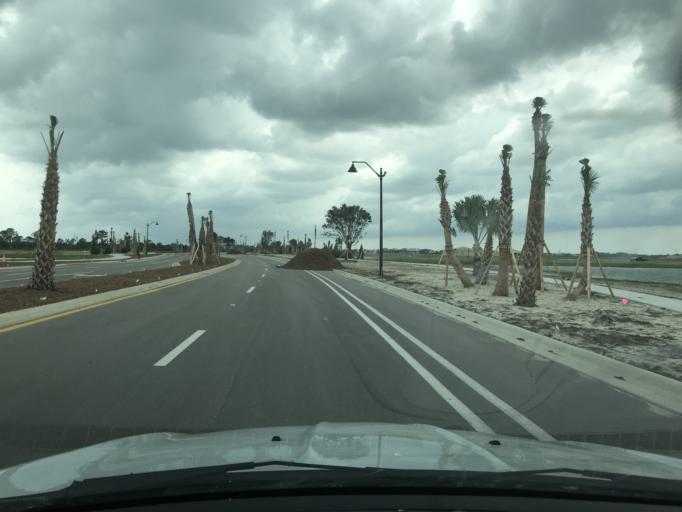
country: US
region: Florida
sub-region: Lee County
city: Olga
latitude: 26.7876
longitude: -81.7320
